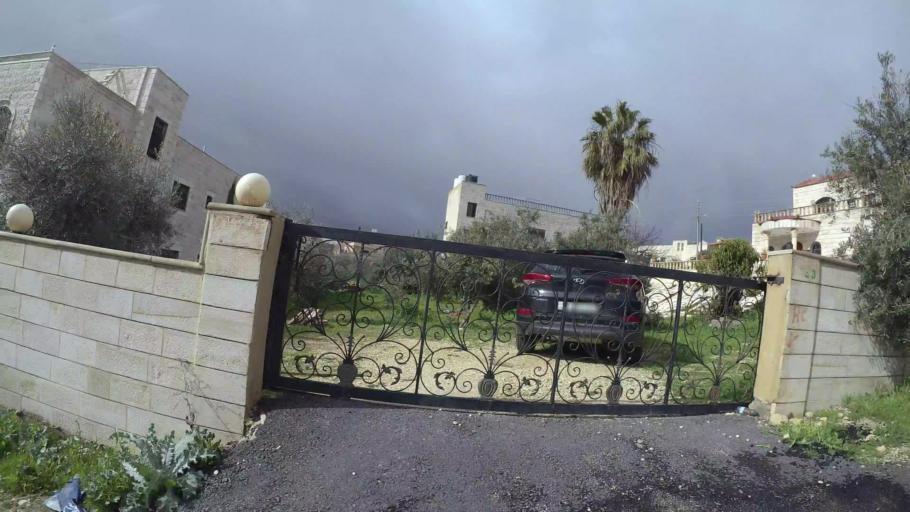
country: JO
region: Amman
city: Al Jubayhah
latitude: 32.0556
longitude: 35.8897
